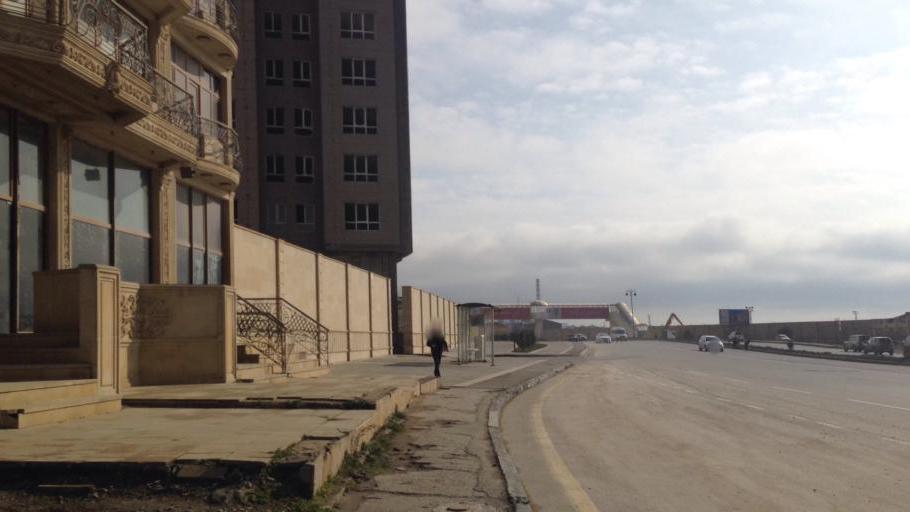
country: AZ
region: Baki
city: Baku
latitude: 40.3789
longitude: 49.8891
